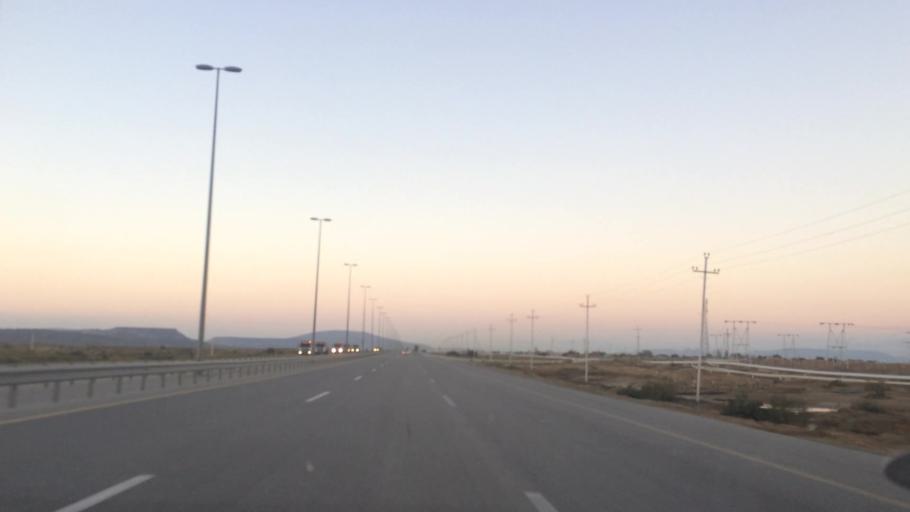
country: AZ
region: Baki
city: Qobustan
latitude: 40.0040
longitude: 49.4290
